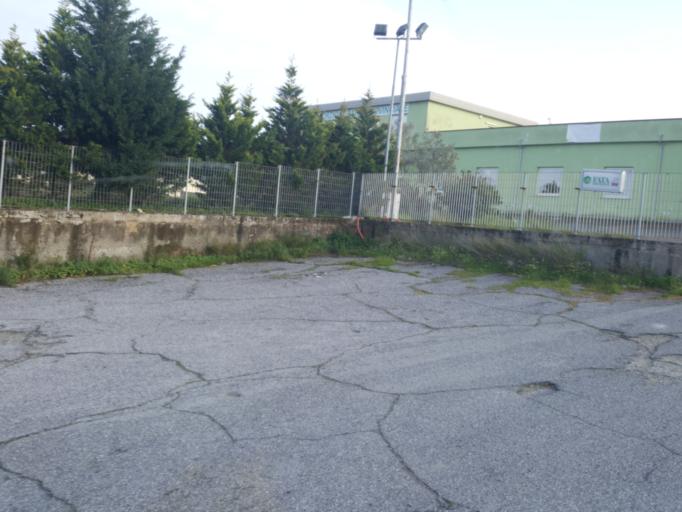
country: IT
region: Calabria
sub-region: Provincia di Catanzaro
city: Roccelletta
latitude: 38.8148
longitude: 16.5842
